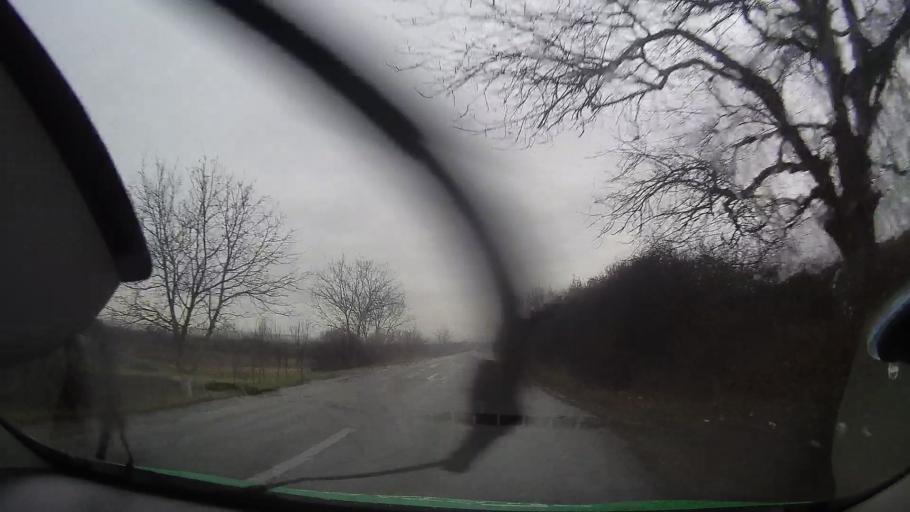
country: RO
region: Bihor
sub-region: Comuna Sambata
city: Sambata
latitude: 46.7785
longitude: 22.1876
